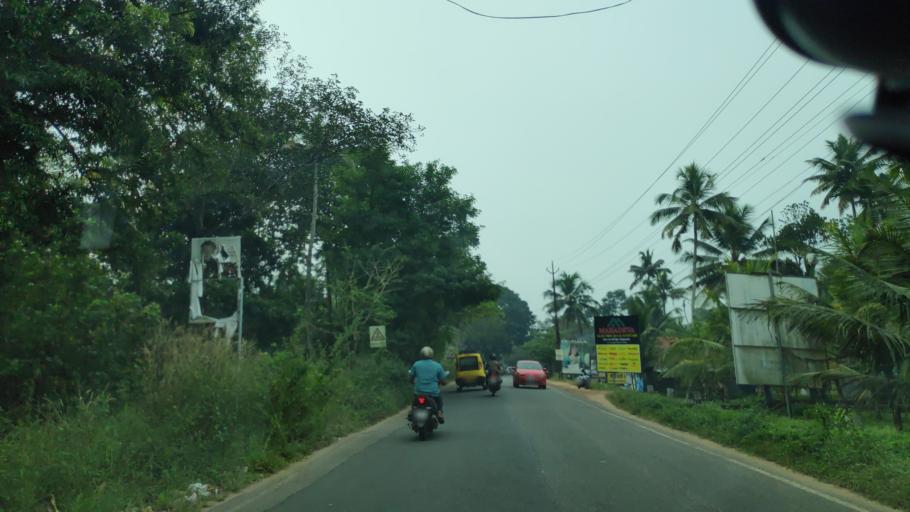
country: IN
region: Kerala
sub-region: Alappuzha
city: Alleppey
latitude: 9.5774
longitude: 76.3490
